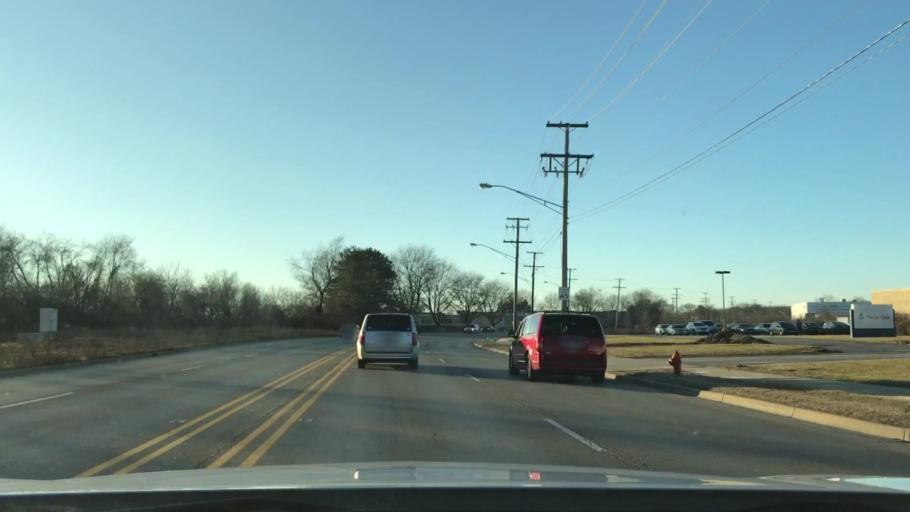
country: US
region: Illinois
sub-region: Kane County
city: Sleepy Hollow
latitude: 42.0584
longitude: -88.3193
